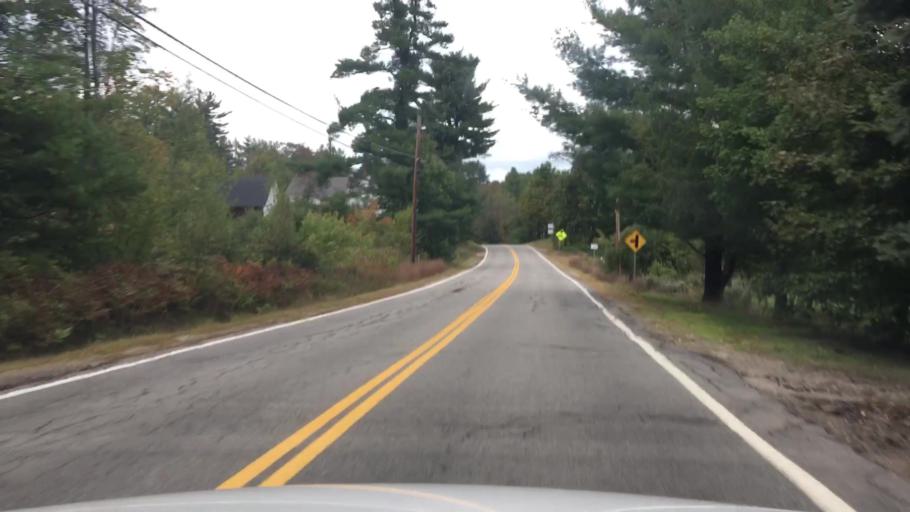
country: US
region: New Hampshire
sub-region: Carroll County
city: Effingham
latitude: 43.7379
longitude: -71.0092
